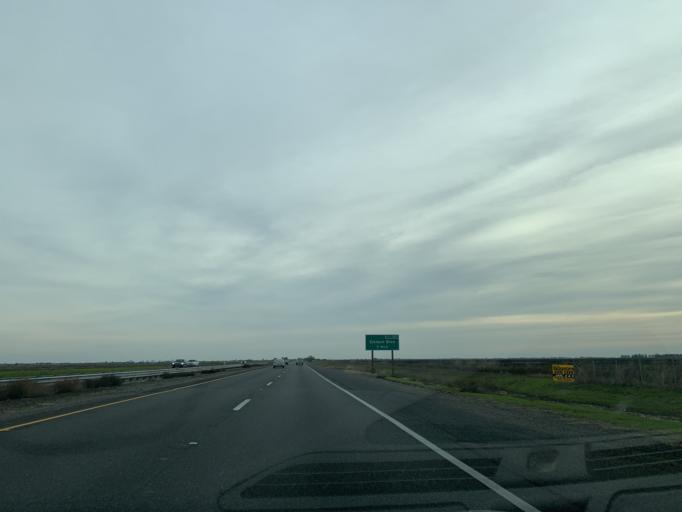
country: US
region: California
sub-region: Sacramento County
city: Elverta
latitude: 38.7045
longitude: -121.5405
